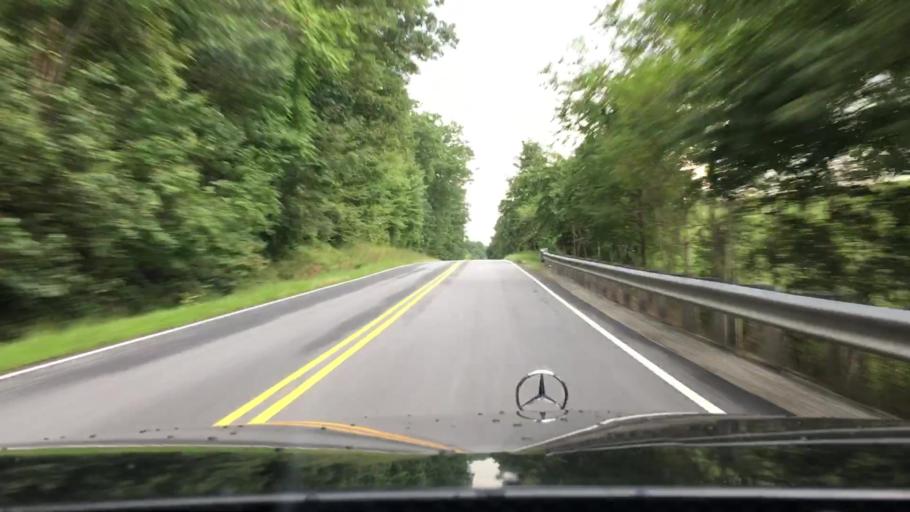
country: US
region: Virginia
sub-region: Nelson County
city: Lovingston
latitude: 37.8081
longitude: -78.9470
